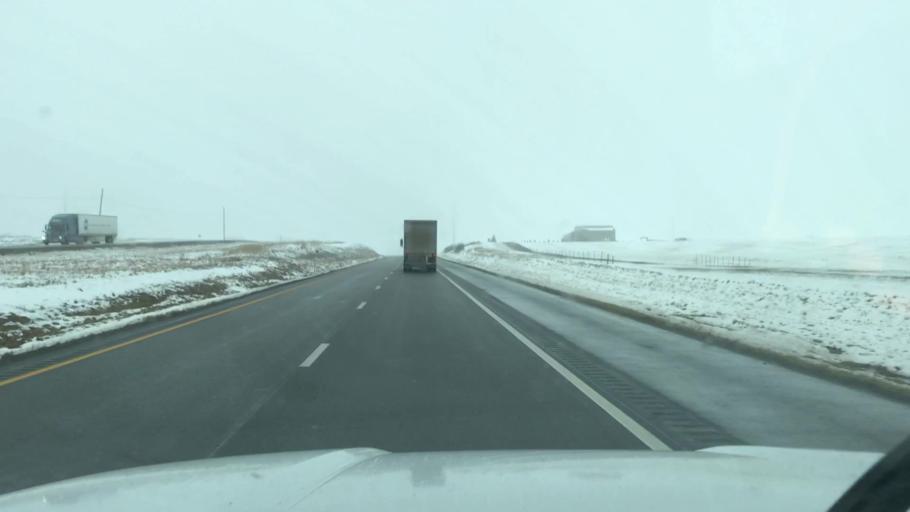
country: US
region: Missouri
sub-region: DeKalb County
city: Maysville
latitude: 39.7621
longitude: -94.4514
